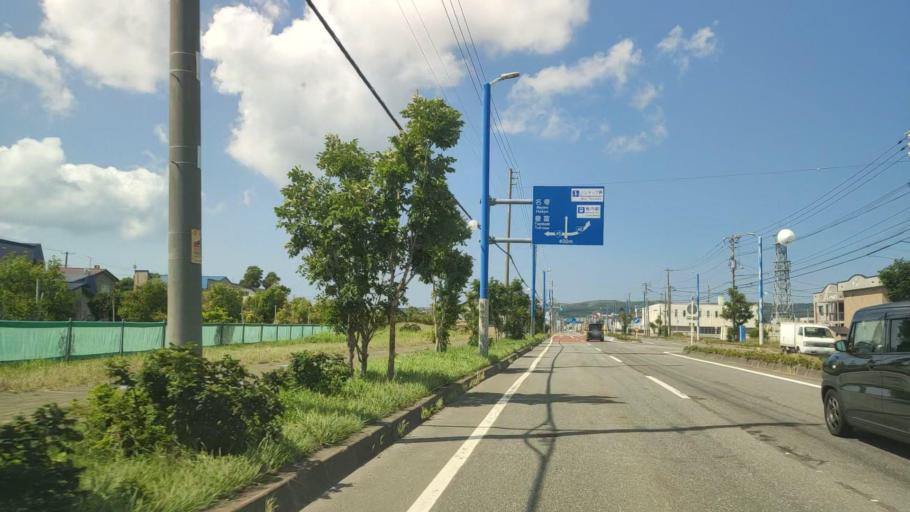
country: JP
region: Hokkaido
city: Wakkanai
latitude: 45.3950
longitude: 141.7129
